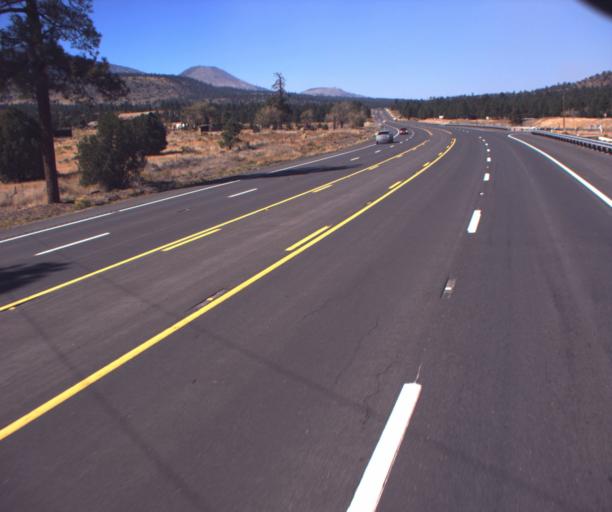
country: US
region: Arizona
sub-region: Coconino County
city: Flagstaff
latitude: 35.3332
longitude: -111.5484
